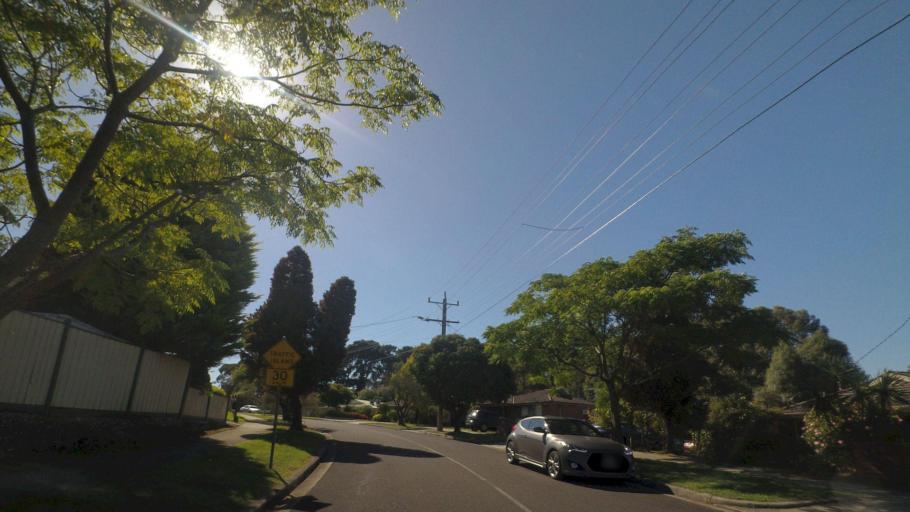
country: AU
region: Victoria
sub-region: Manningham
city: Donvale
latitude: -37.7801
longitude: 145.1736
